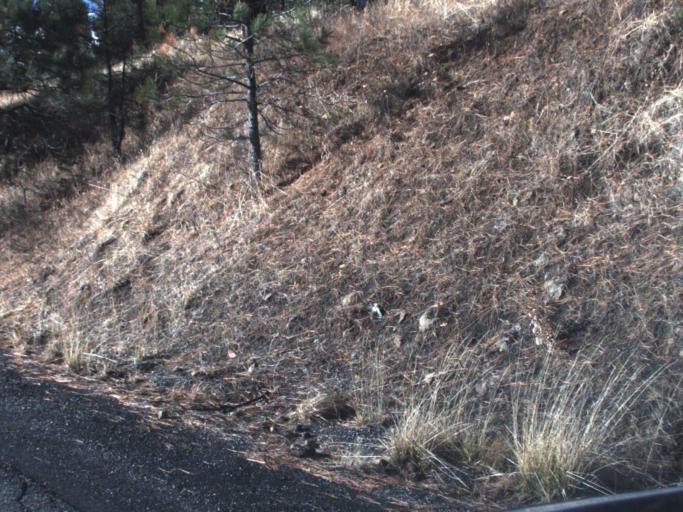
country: US
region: Washington
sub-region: Asotin County
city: Asotin
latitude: 46.0909
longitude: -117.1585
